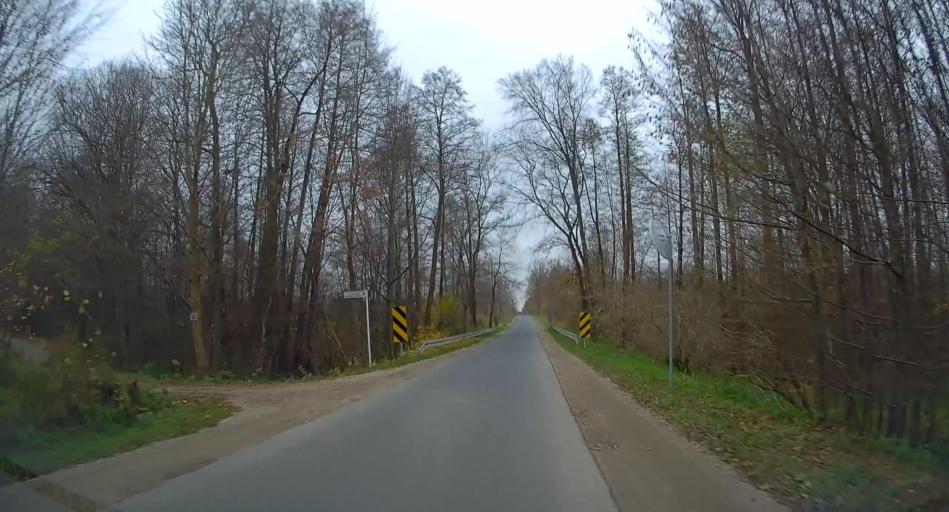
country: PL
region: Lodz Voivodeship
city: Zabia Wola
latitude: 51.9987
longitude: 20.6586
